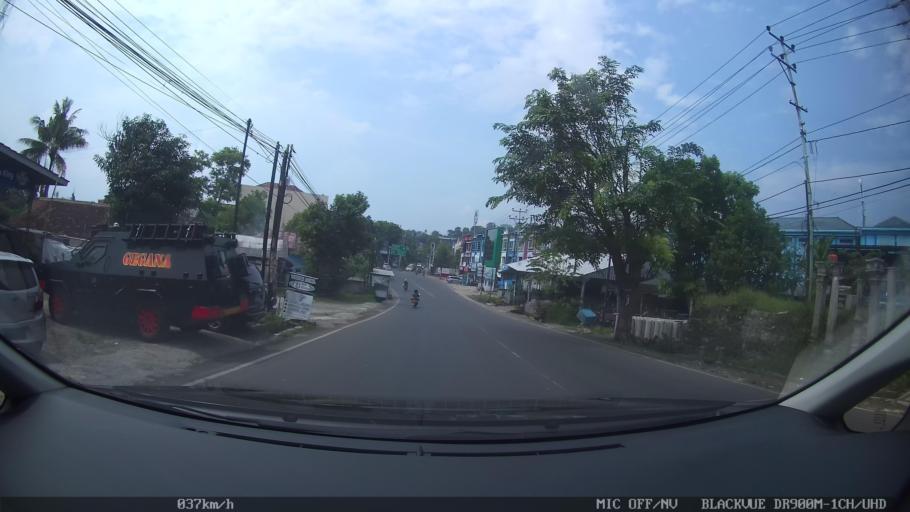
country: ID
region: Lampung
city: Bandarlampung
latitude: -5.4178
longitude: 105.2467
